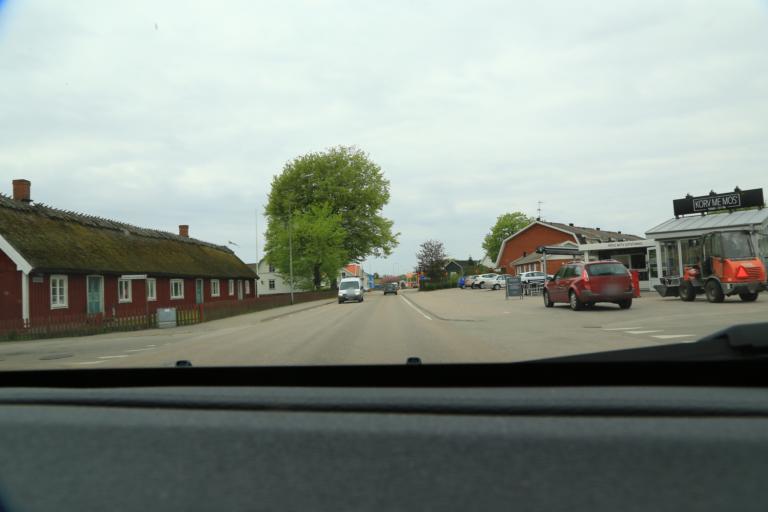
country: SE
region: Halland
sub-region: Varbergs Kommun
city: Tvaaker
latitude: 57.0427
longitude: 12.3971
